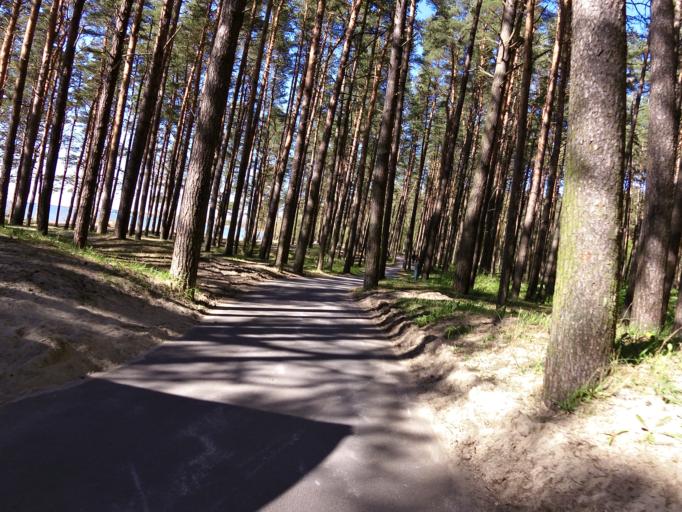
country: EE
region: Harju
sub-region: Viimsi vald
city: Viimsi
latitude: 59.4746
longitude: 24.8343
